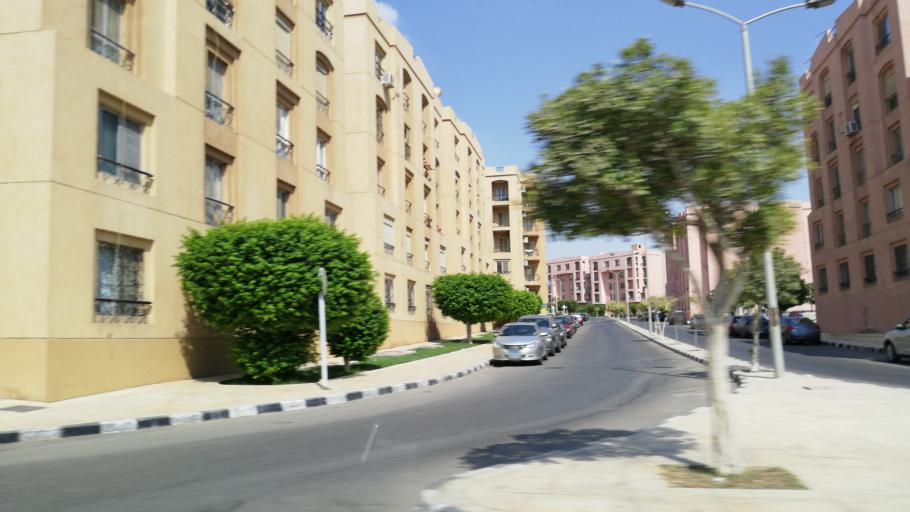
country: EG
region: Muhafazat al Qalyubiyah
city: Al Khankah
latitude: 30.0603
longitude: 31.4877
